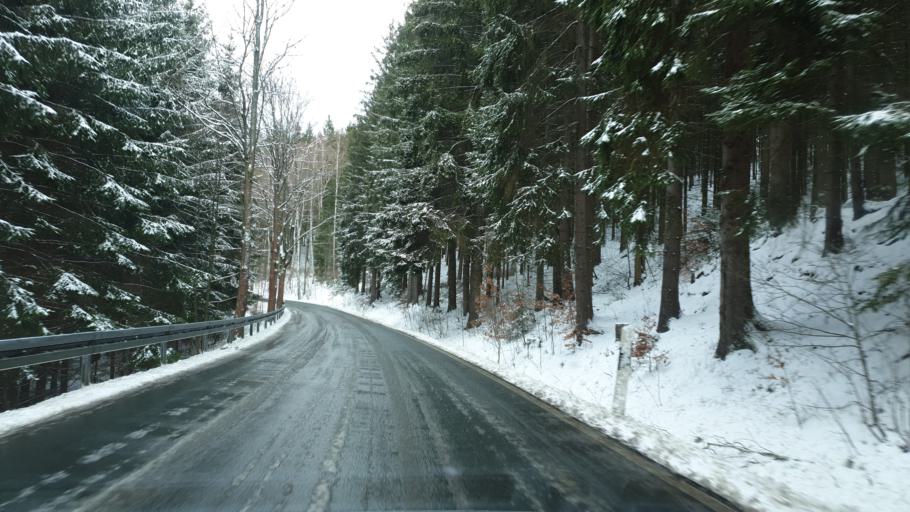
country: DE
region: Saxony
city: Bad Elster
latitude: 50.2696
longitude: 12.2501
